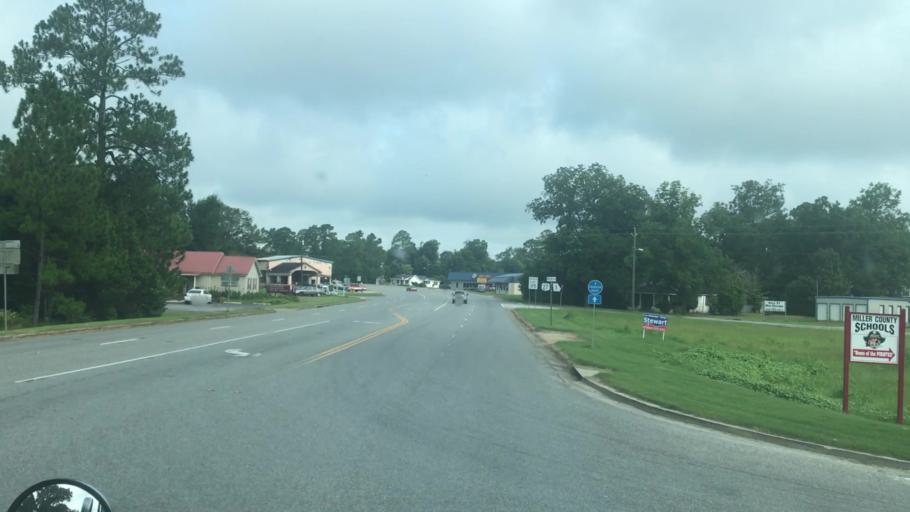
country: US
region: Georgia
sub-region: Miller County
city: Colquitt
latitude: 31.1677
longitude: -84.7251
